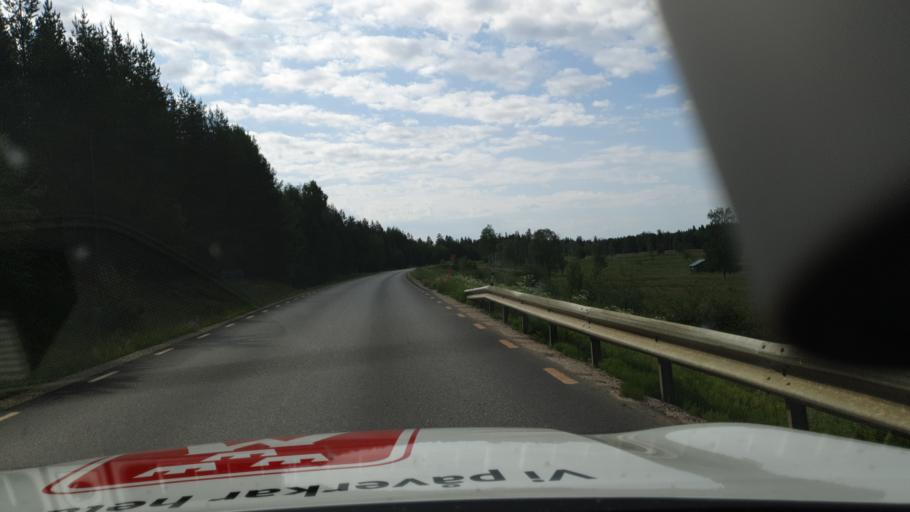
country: SE
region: Vaesterbotten
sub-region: Norsjo Kommun
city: Norsjoe
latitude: 64.5178
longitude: 19.3462
